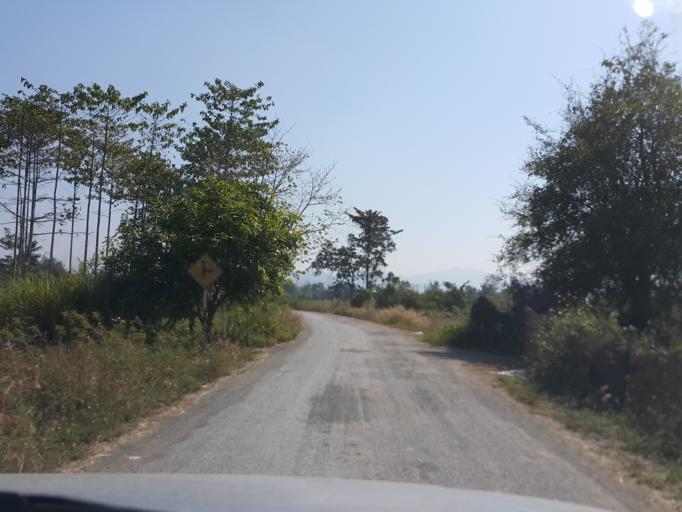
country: TH
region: Chiang Mai
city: San Kamphaeng
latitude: 18.8362
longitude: 99.1426
